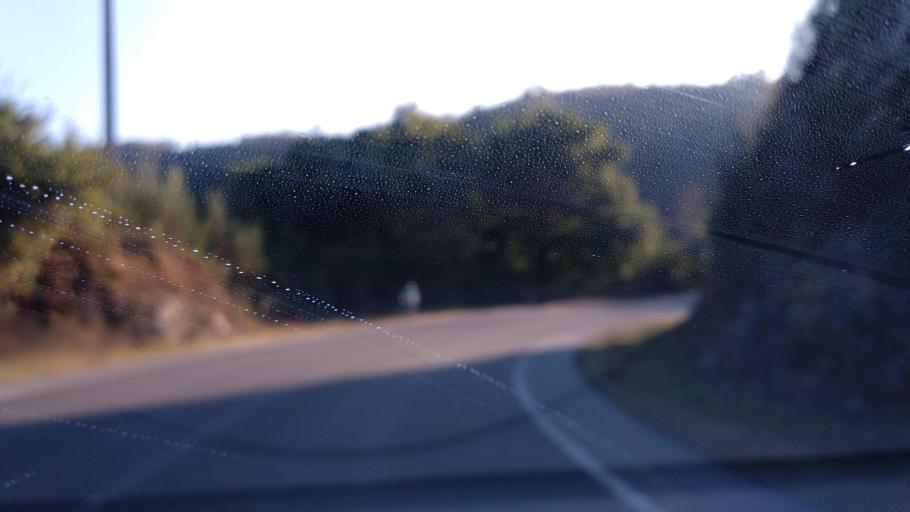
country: ES
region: Galicia
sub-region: Provincia de Pontevedra
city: Ponte Caldelas
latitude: 42.3377
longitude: -8.5500
